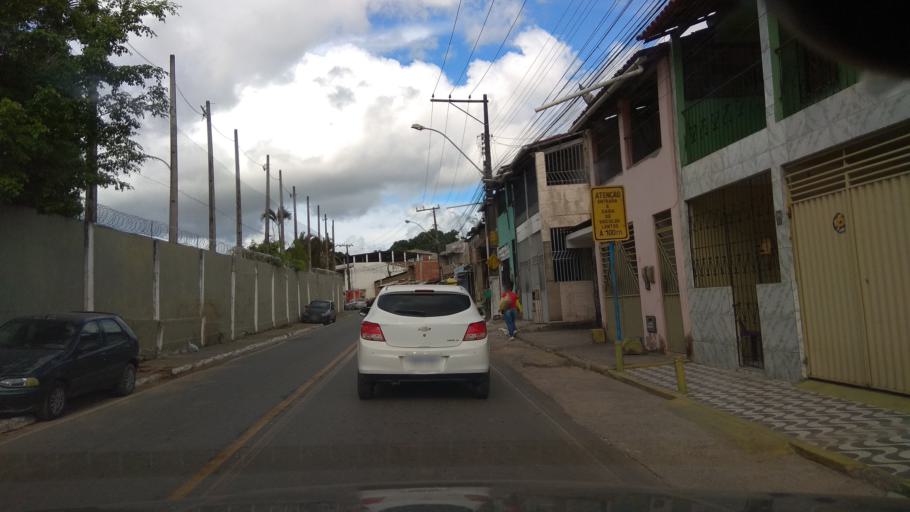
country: BR
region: Bahia
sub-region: Ilheus
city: Ilheus
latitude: -14.7933
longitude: -39.0633
